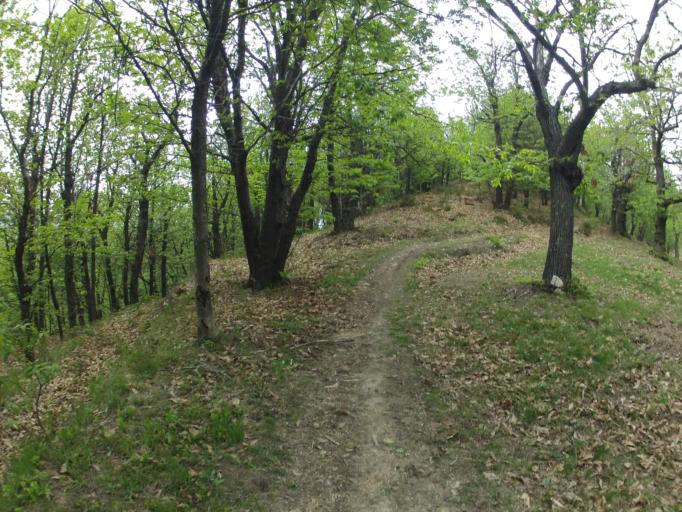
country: IT
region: Piedmont
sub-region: Provincia di Cuneo
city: Peveragno
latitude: 44.3197
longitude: 7.5835
